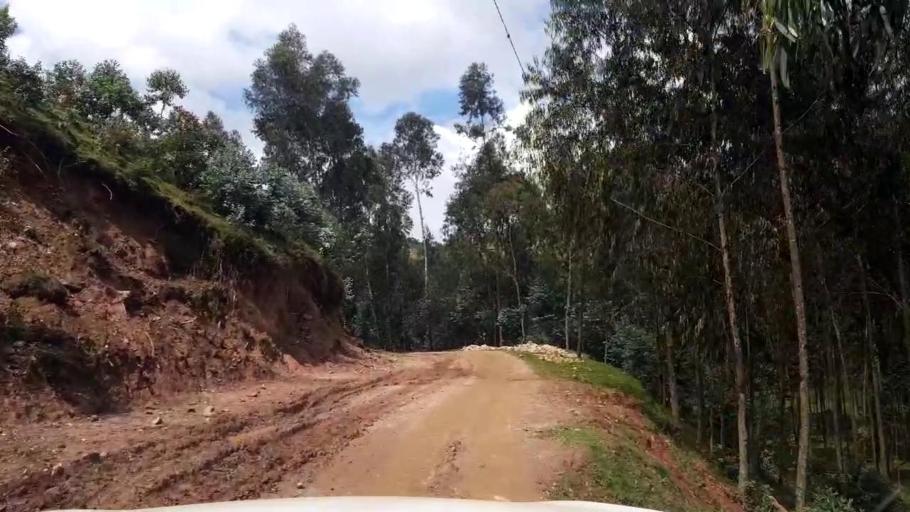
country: RW
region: Western Province
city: Kibuye
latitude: -1.9102
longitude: 29.4573
